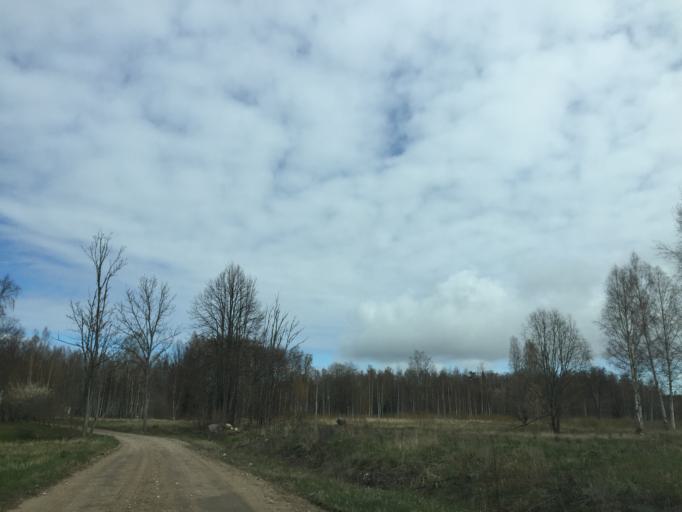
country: LV
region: Salacgrivas
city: Salacgriva
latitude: 57.5383
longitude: 24.3693
